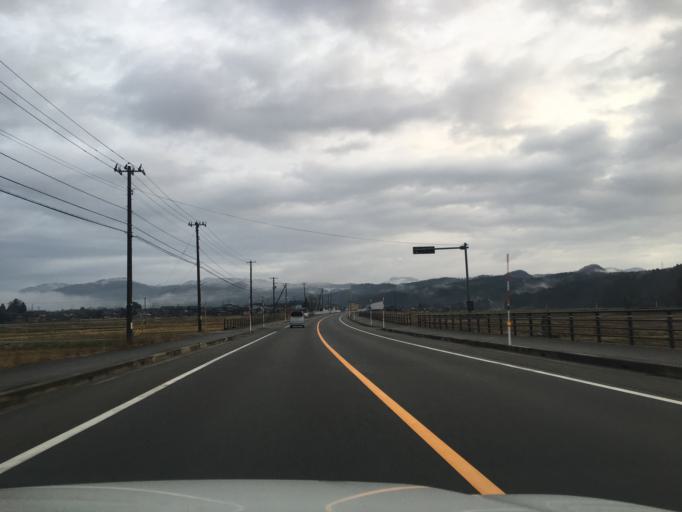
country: JP
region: Niigata
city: Murakami
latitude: 38.3197
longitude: 139.5524
